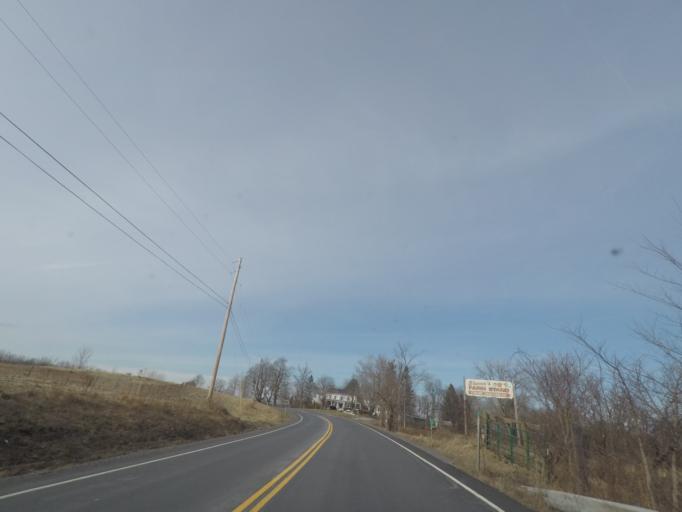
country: US
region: New York
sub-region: Columbia County
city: Valatie
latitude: 42.3937
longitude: -73.6440
